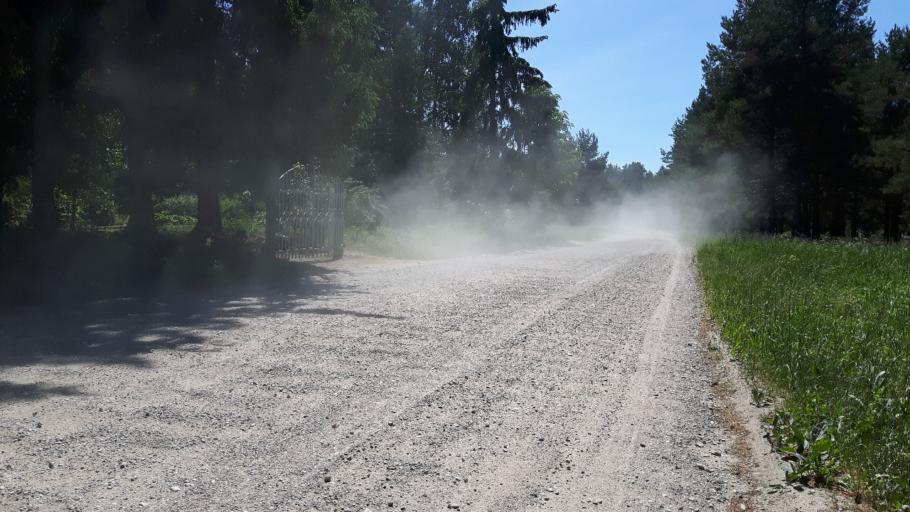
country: LV
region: Kandava
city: Kandava
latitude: 57.0379
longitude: 22.8017
